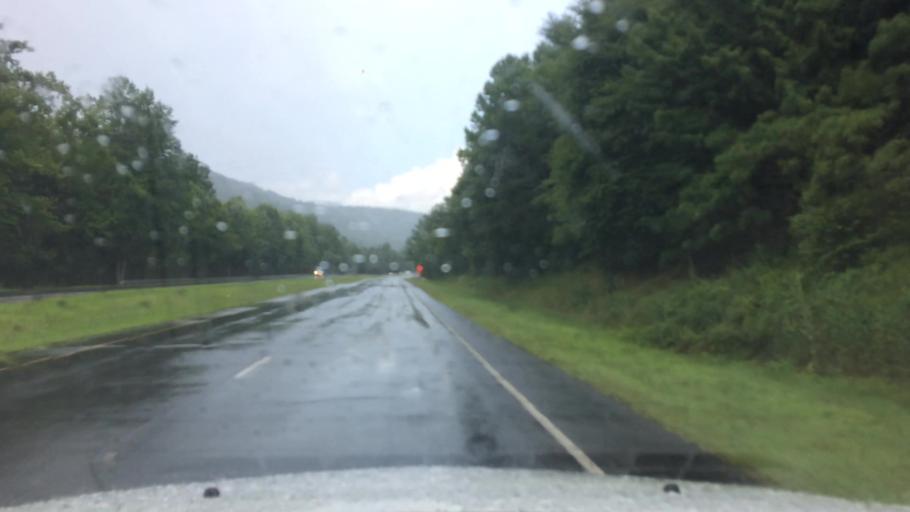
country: US
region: North Carolina
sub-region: Wilkes County
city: Millers Creek
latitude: 36.1928
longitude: -81.4151
